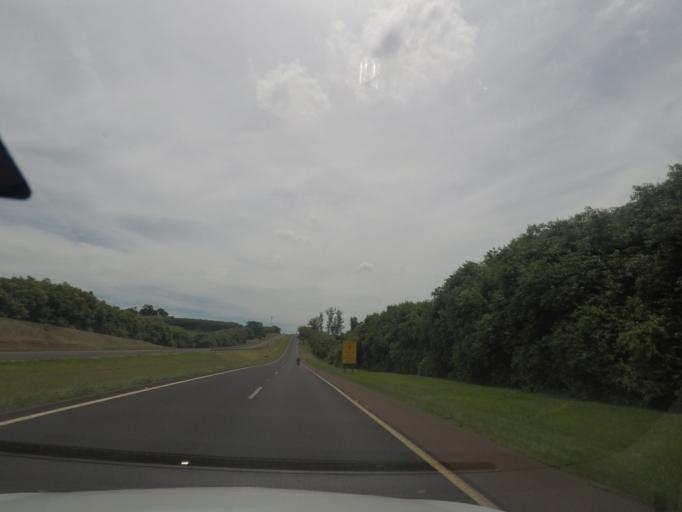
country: BR
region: Sao Paulo
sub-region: Bebedouro
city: Bebedouro
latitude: -20.9997
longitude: -48.4307
